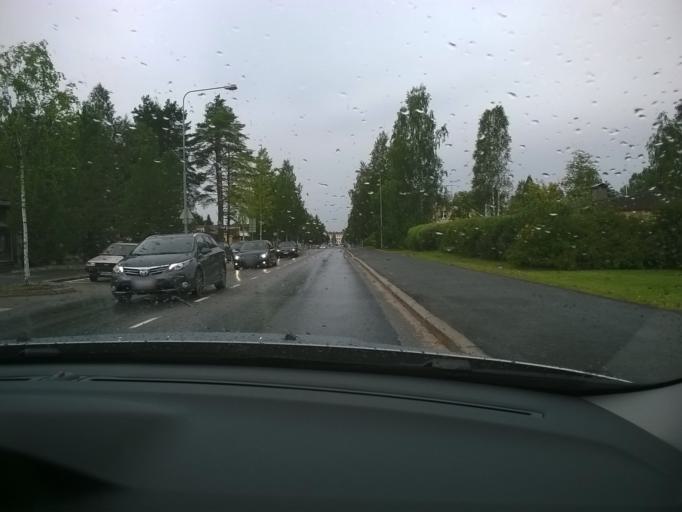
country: FI
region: Kainuu
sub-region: Kehys-Kainuu
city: Kuhmo
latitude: 64.1251
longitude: 29.5299
